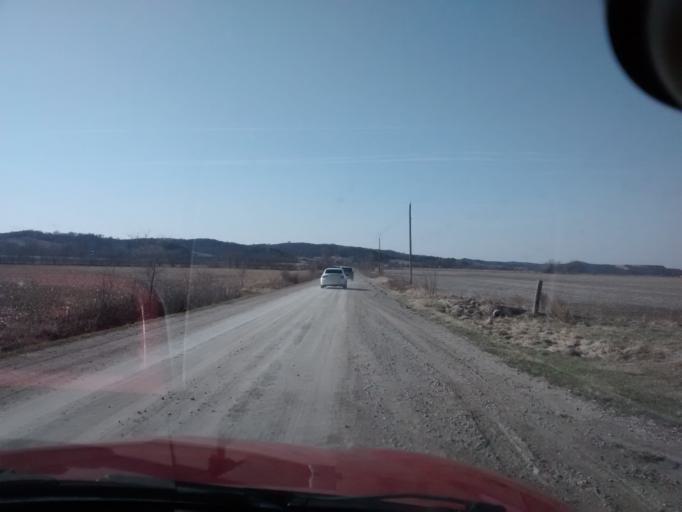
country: US
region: Iowa
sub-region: Pottawattamie County
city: Carter Lake
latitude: 41.3976
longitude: -95.8508
